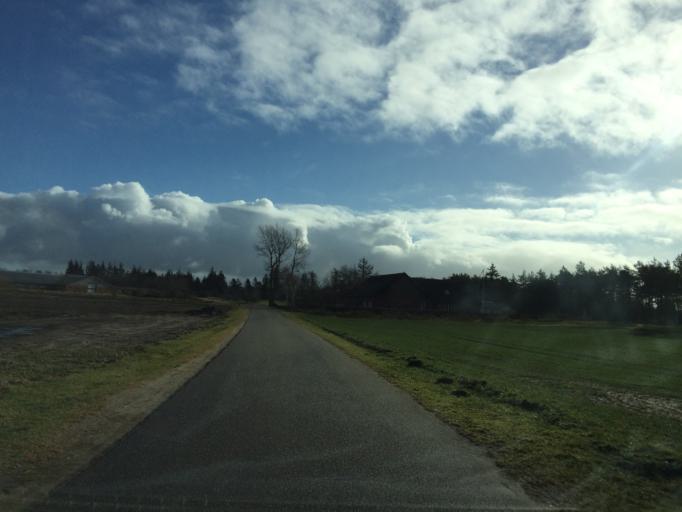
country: DK
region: Central Jutland
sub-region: Holstebro Kommune
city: Ulfborg
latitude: 56.2796
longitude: 8.3496
